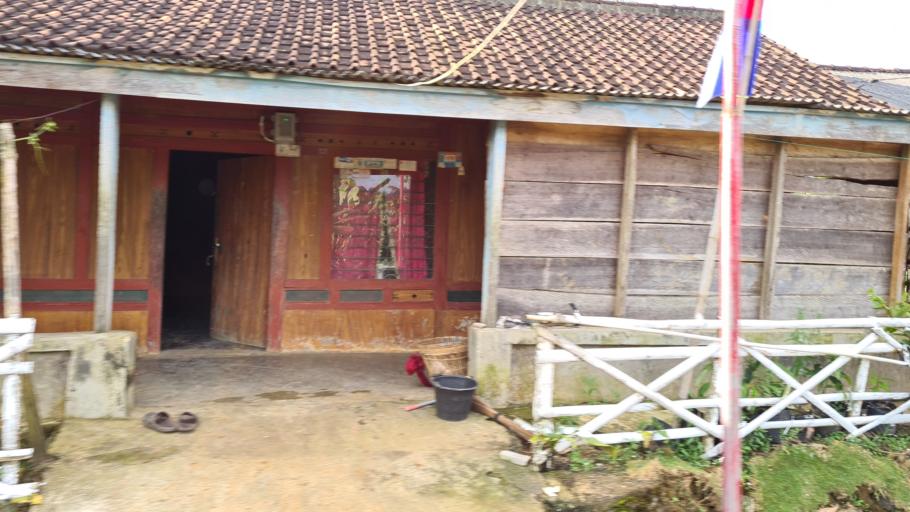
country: ID
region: Lampung
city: Kenali
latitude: -5.0933
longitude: 104.3998
